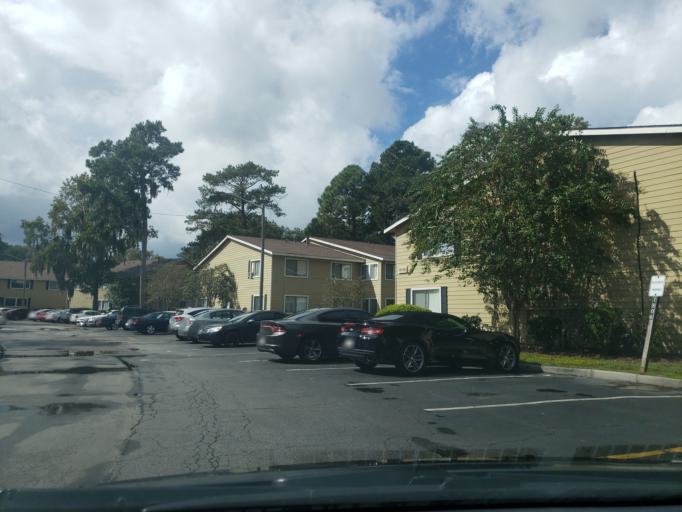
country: US
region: Georgia
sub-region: Chatham County
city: Isle of Hope
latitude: 32.0088
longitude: -81.1035
